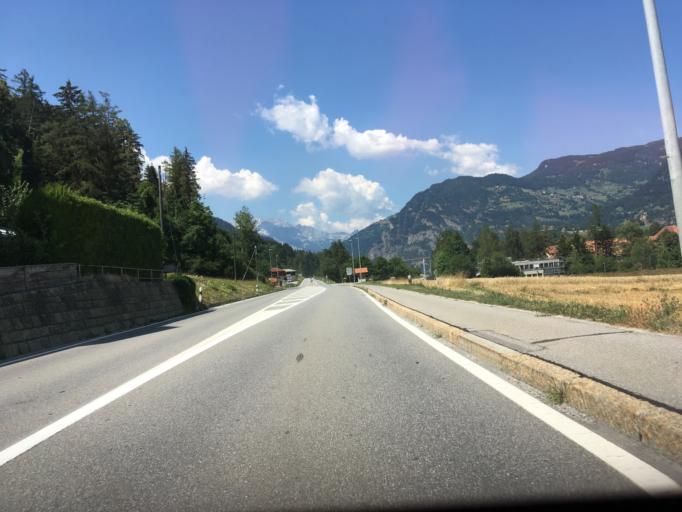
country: CH
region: Grisons
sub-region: Hinterrhein District
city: Cazis
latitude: 46.7279
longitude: 9.4267
